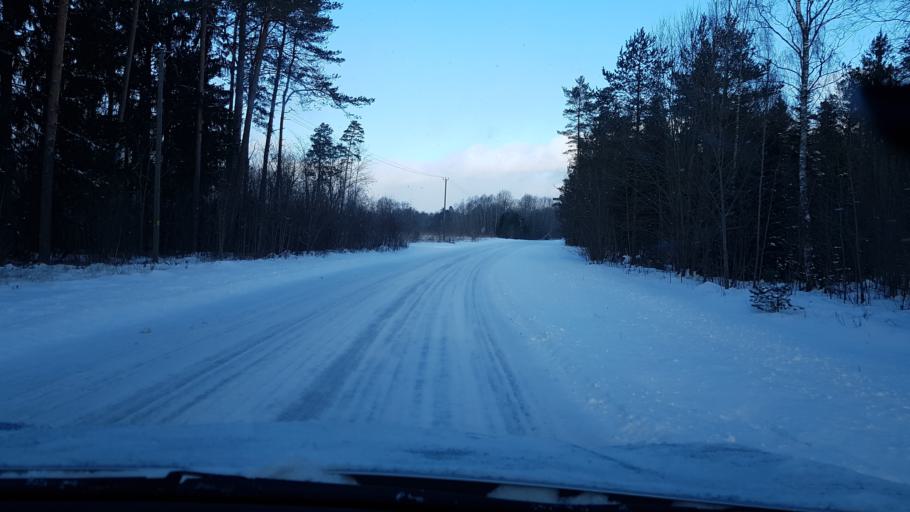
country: EE
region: Harju
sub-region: Nissi vald
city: Turba
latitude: 59.2193
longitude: 24.1400
